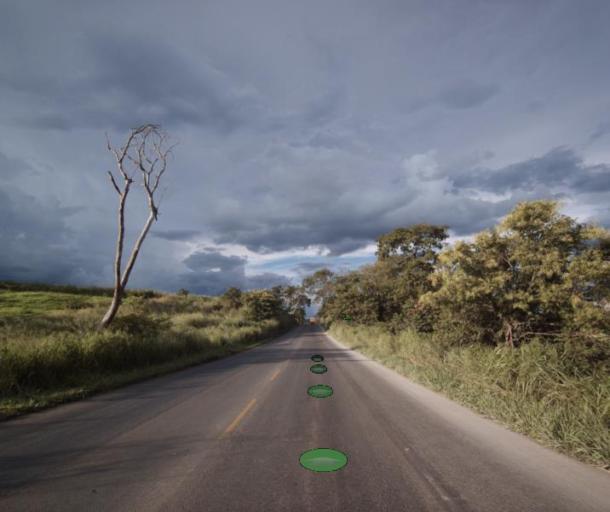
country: BR
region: Goias
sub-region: Itapaci
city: Itapaci
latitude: -15.0931
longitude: -49.4719
